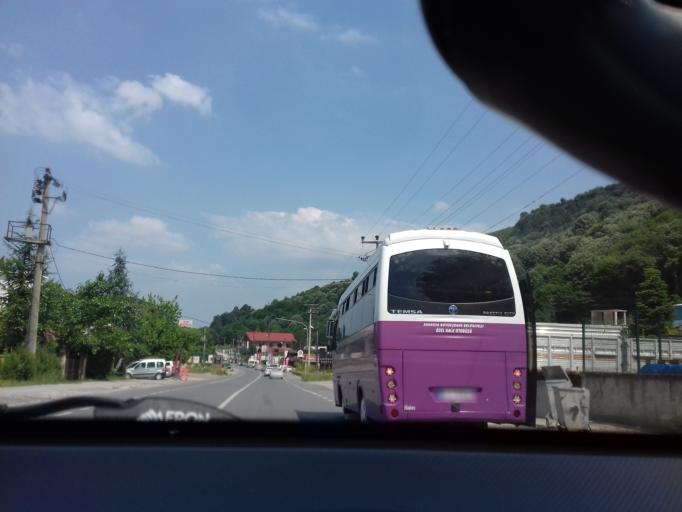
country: TR
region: Sakarya
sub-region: Merkez
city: Sapanca
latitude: 40.6909
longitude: 30.2192
